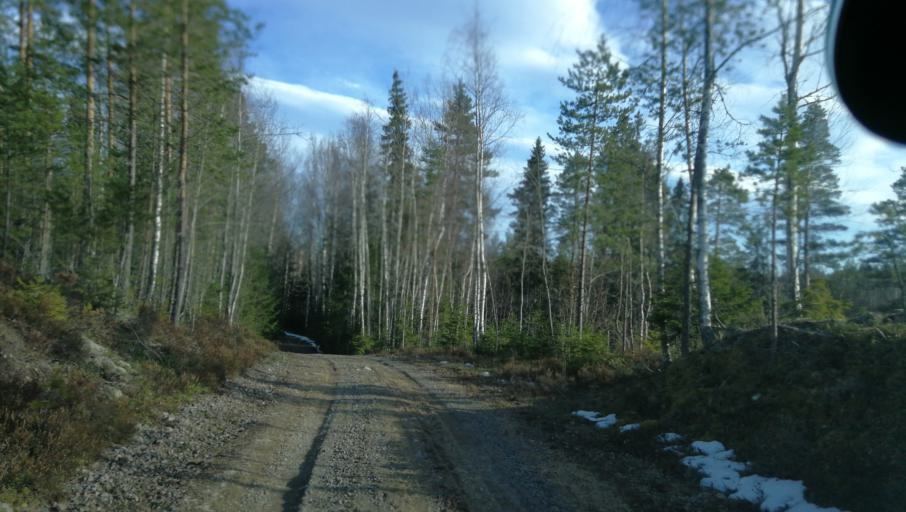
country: SE
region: Dalarna
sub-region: Vansbro Kommun
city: Vansbro
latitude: 60.7959
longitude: 14.2327
